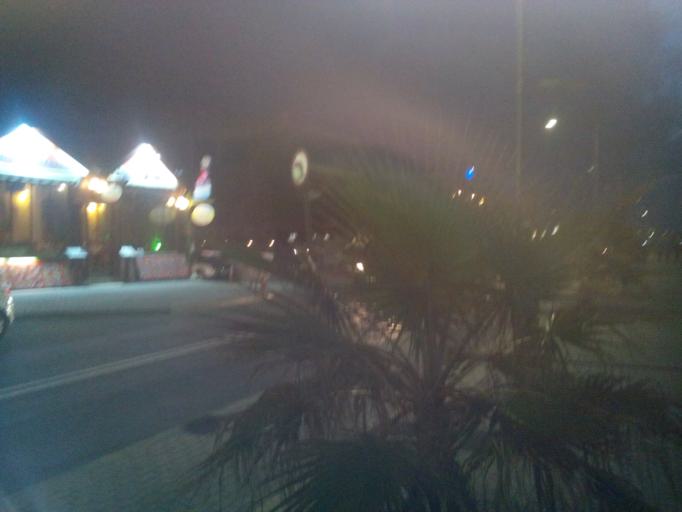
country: GR
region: Crete
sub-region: Nomos Rethymnis
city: Rethymno
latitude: 35.3673
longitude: 24.4964
